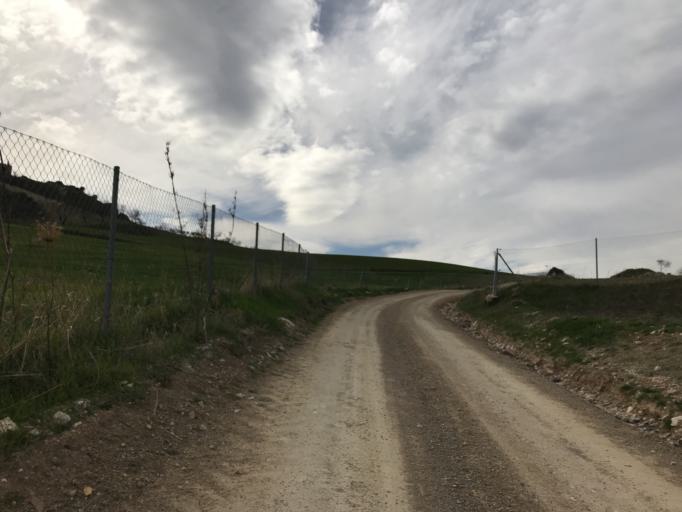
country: ES
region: Andalusia
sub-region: Provincia de Malaga
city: Ardales
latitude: 36.8738
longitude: -4.8794
